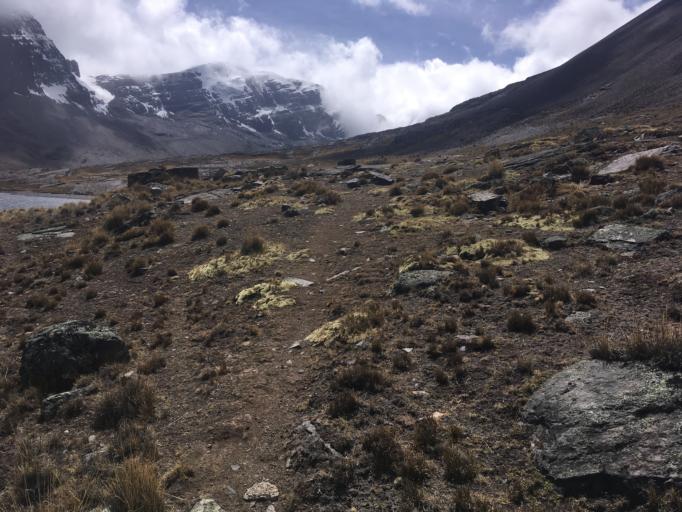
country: BO
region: La Paz
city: La Paz
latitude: -16.3973
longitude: -67.9703
